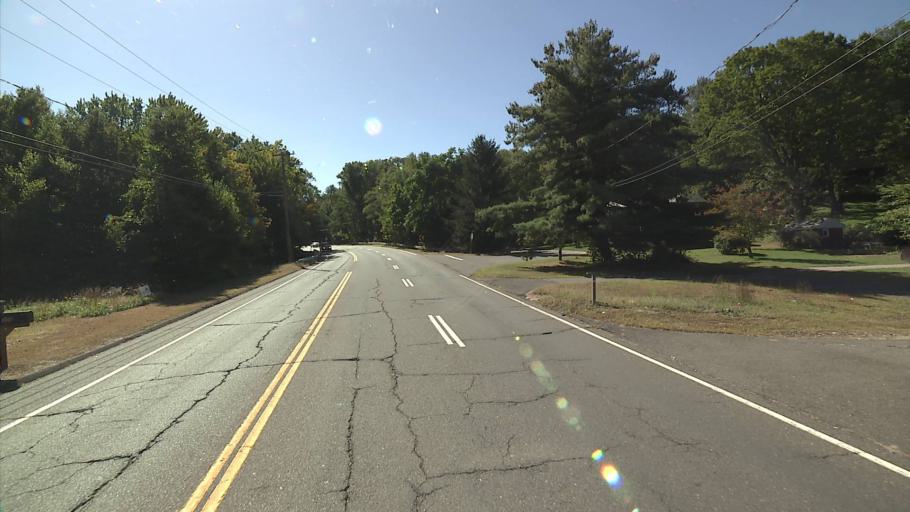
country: US
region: Connecticut
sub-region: New Haven County
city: Prospect
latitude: 41.5334
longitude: -73.0103
